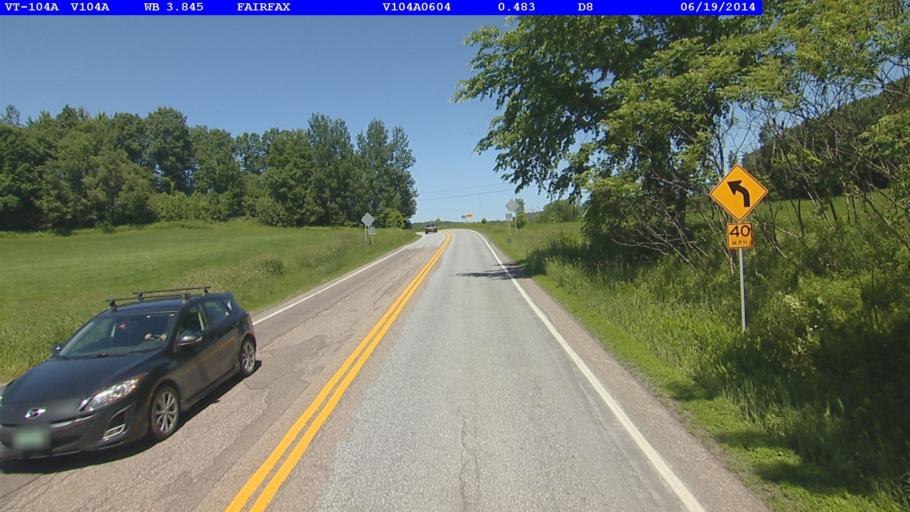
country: US
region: Vermont
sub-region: Chittenden County
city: Milton
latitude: 44.6813
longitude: -73.0412
